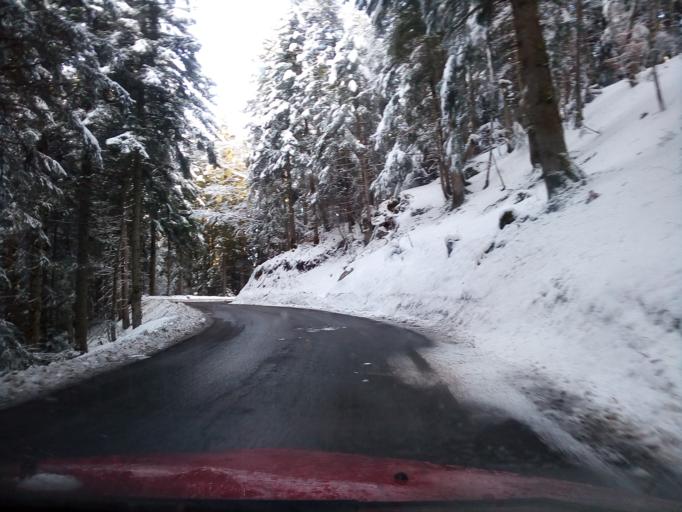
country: FR
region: Rhone-Alpes
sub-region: Departement de l'Isere
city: Le Sappey-en-Chartreuse
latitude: 45.3096
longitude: 5.7712
